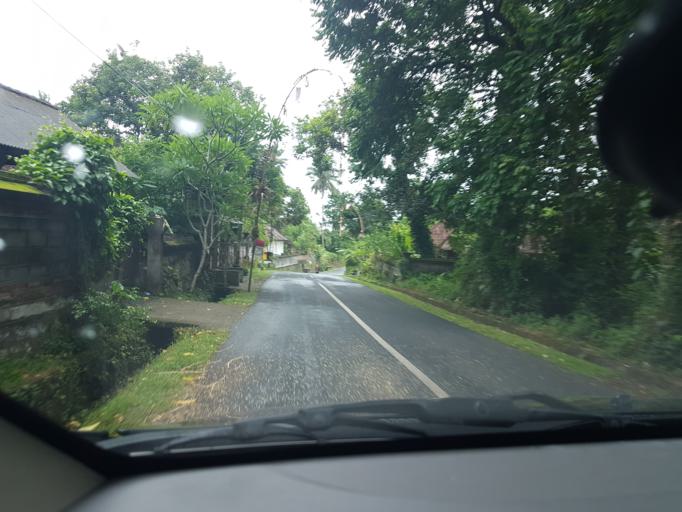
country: ID
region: Bali
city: Banjar Tebongkang
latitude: -8.5304
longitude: 115.2372
